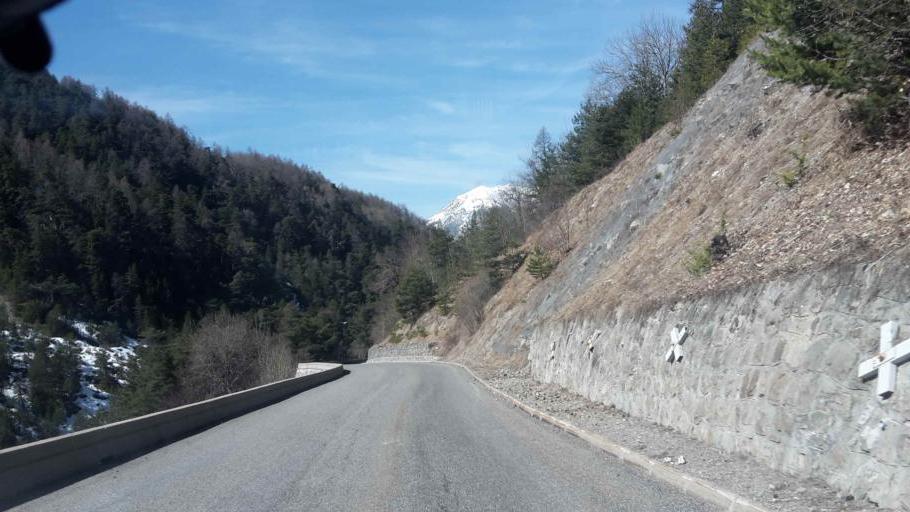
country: FR
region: Provence-Alpes-Cote d'Azur
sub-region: Departement des Hautes-Alpes
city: Embrun
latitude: 44.5507
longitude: 6.5814
